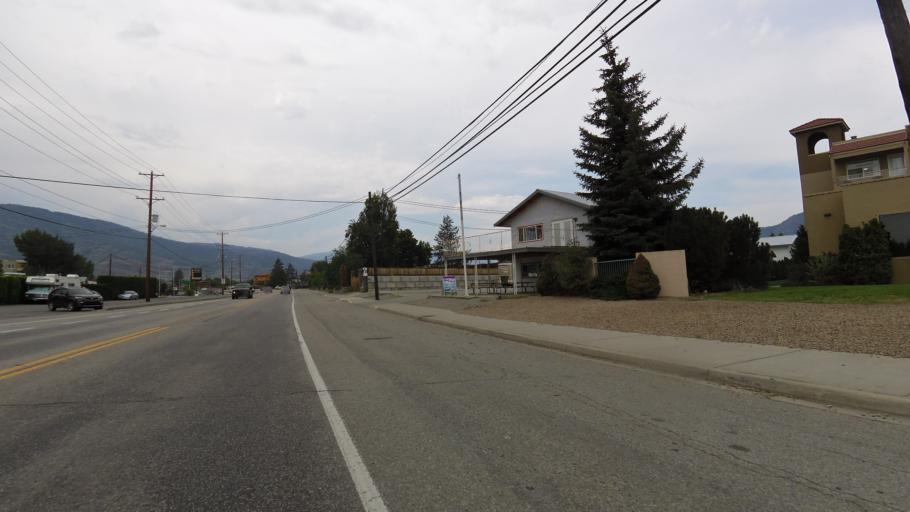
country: CA
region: British Columbia
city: Osoyoos
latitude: 49.0284
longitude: -119.4436
